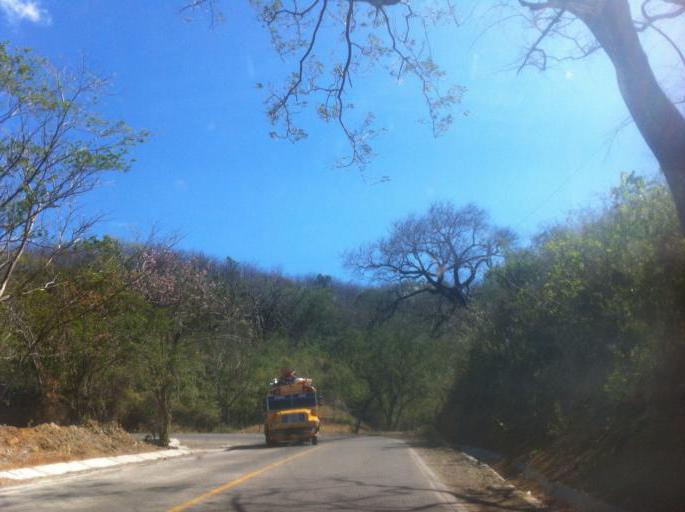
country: NI
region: Rivas
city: Tola
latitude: 11.3917
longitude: -85.9863
